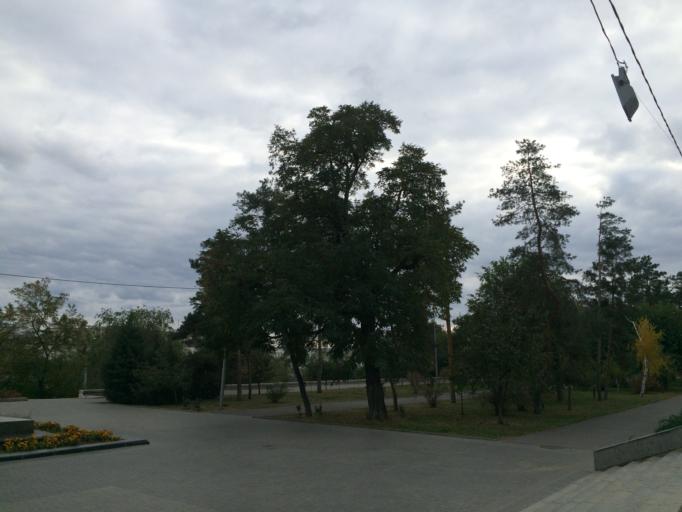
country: RU
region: Volgograd
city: Volgograd
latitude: 48.7021
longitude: 44.5178
